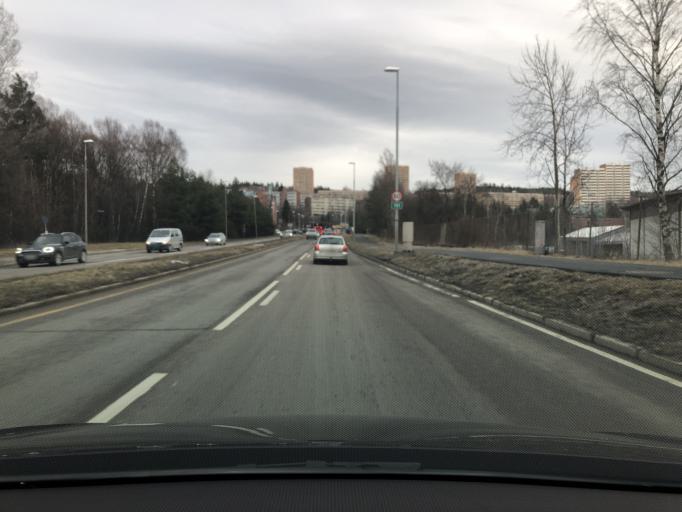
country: NO
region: Akershus
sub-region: Lorenskog
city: Kjenn
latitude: 59.9315
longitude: 10.8612
